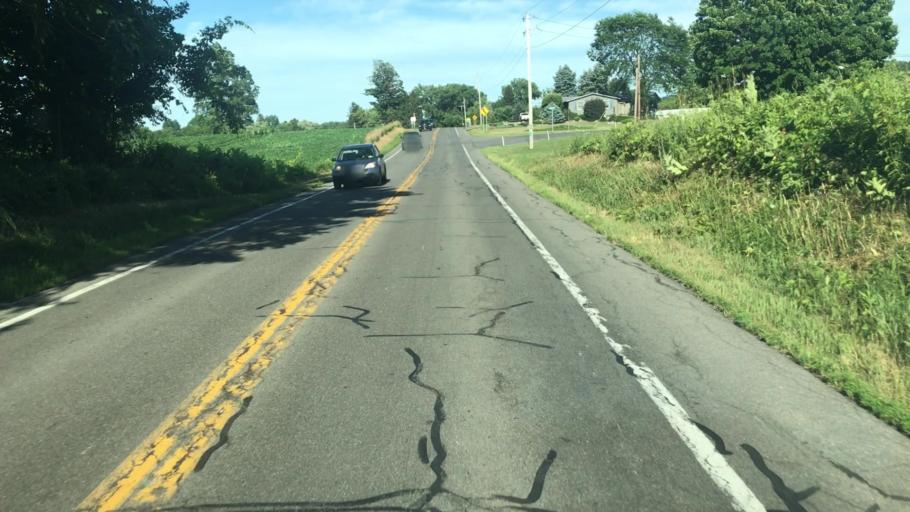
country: US
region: New York
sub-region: Onondaga County
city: Elbridge
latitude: 43.0170
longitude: -76.3961
